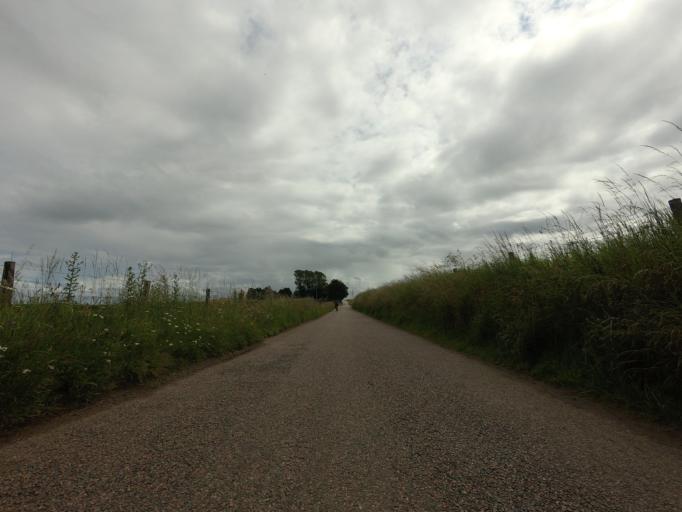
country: GB
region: Scotland
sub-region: Moray
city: Fochabers
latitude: 57.6671
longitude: -3.1516
